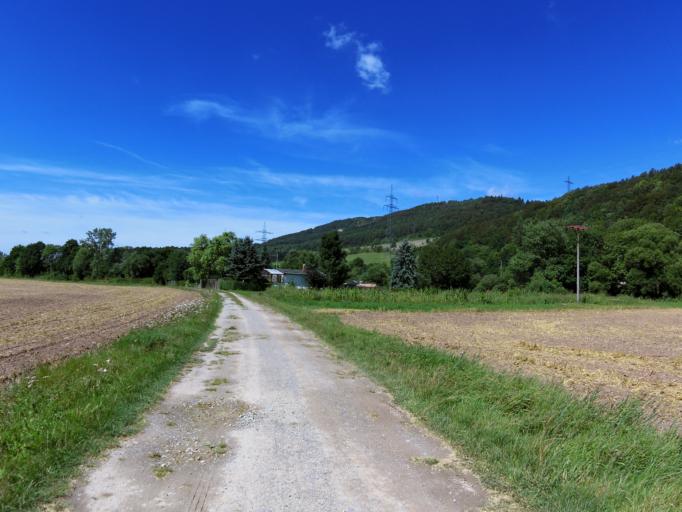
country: DE
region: Thuringia
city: Krauthausen
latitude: 51.0078
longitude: 10.2221
